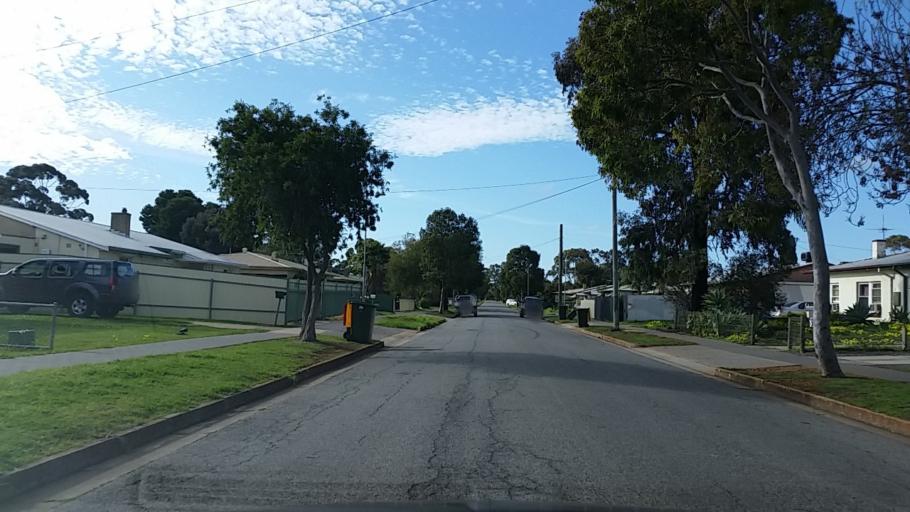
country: AU
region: South Australia
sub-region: Salisbury
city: Elizabeth
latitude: -34.7324
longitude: 138.6651
